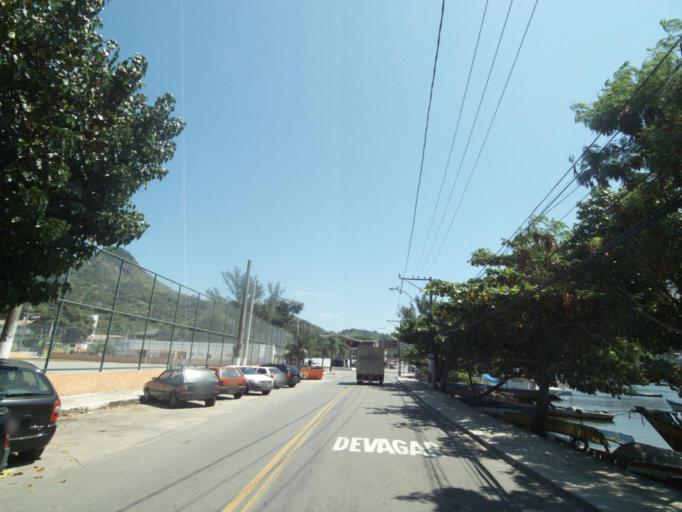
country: BR
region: Rio de Janeiro
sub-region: Niteroi
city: Niteroi
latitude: -22.9351
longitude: -43.1125
